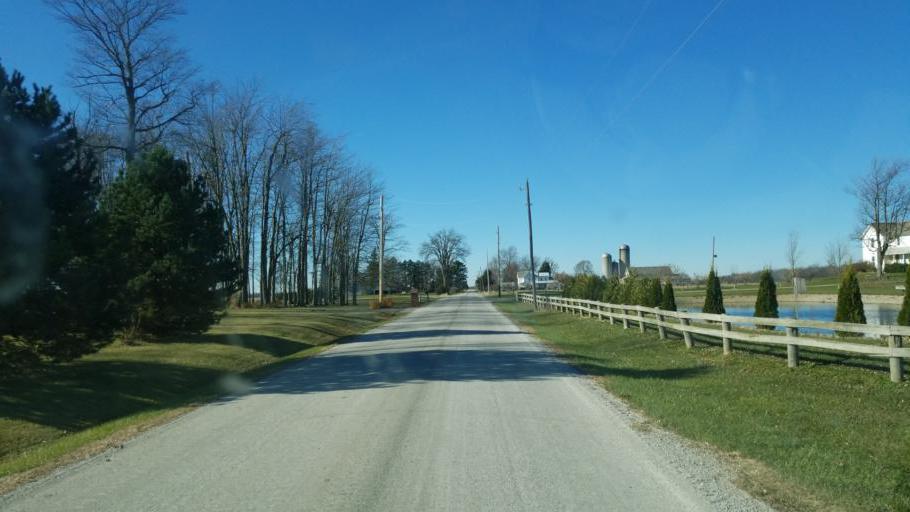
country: US
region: Ohio
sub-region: Huron County
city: Greenwich
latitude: 40.9536
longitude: -82.4725
